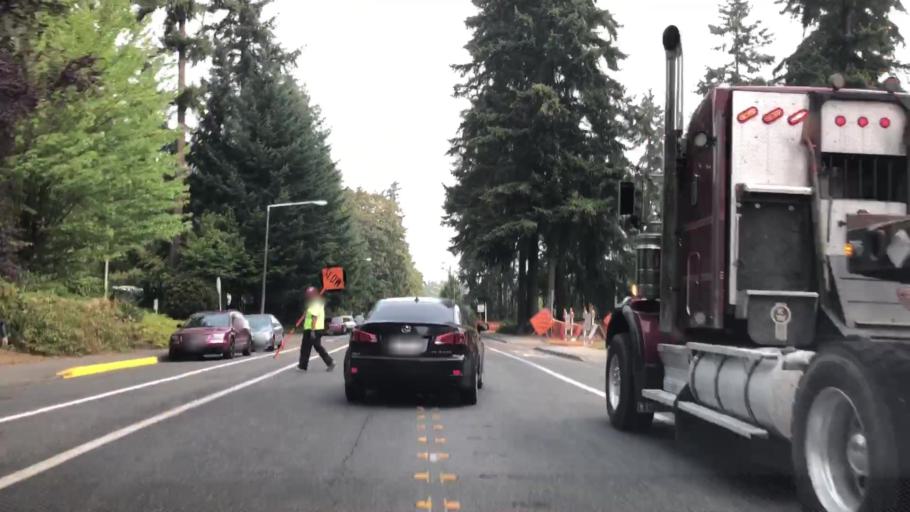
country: US
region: Washington
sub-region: King County
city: Redmond
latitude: 47.6484
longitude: -122.1405
